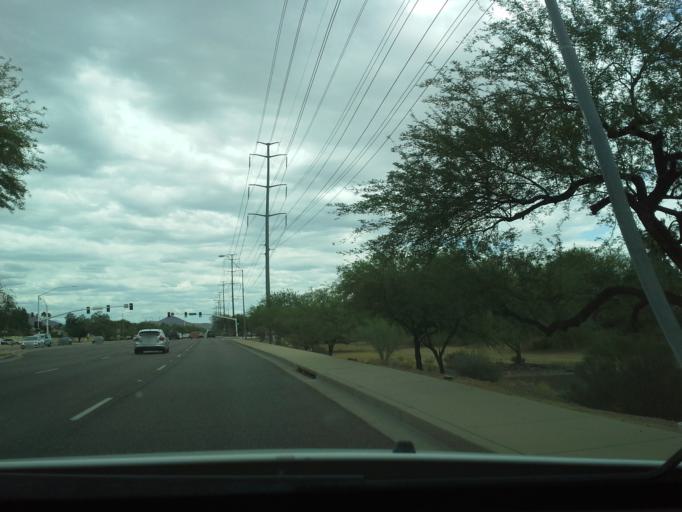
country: US
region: Arizona
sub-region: Maricopa County
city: Scottsdale
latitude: 33.5824
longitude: -111.8540
